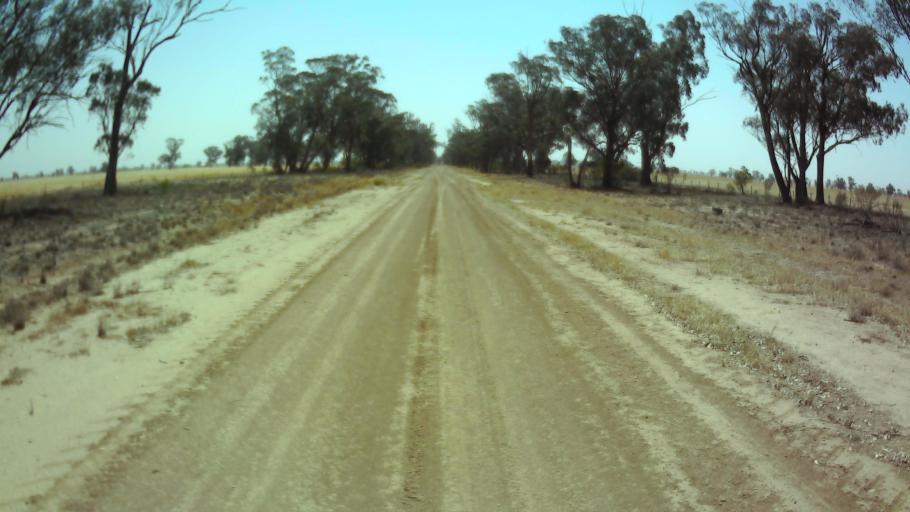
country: AU
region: New South Wales
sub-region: Weddin
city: Grenfell
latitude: -33.9298
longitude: 147.7958
